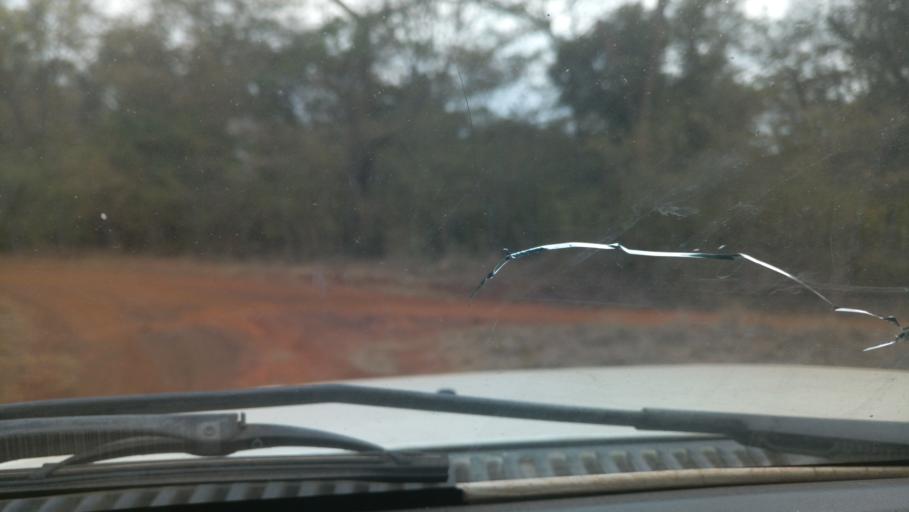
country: KE
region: Nairobi Area
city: Nairobi
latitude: -1.3626
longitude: 36.7828
